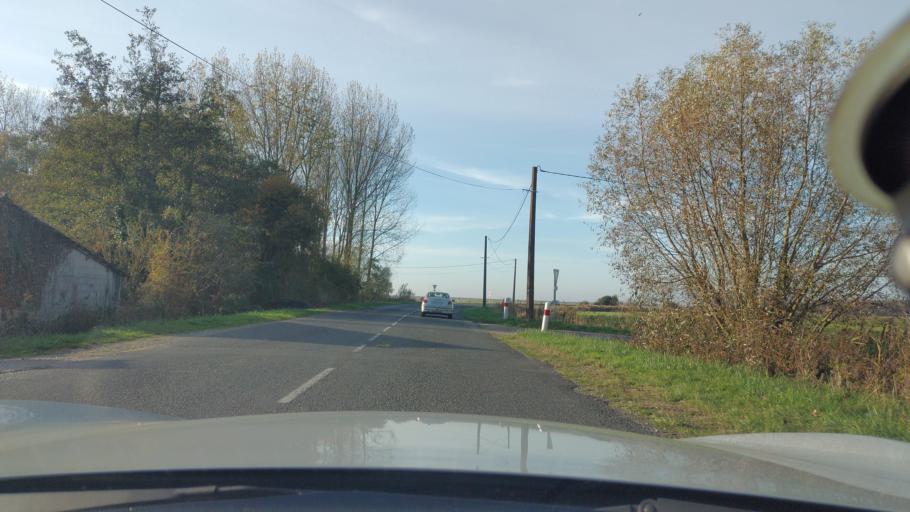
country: FR
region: Picardie
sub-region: Departement de la Somme
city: Cayeux-sur-Mer
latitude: 50.1469
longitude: 1.5096
